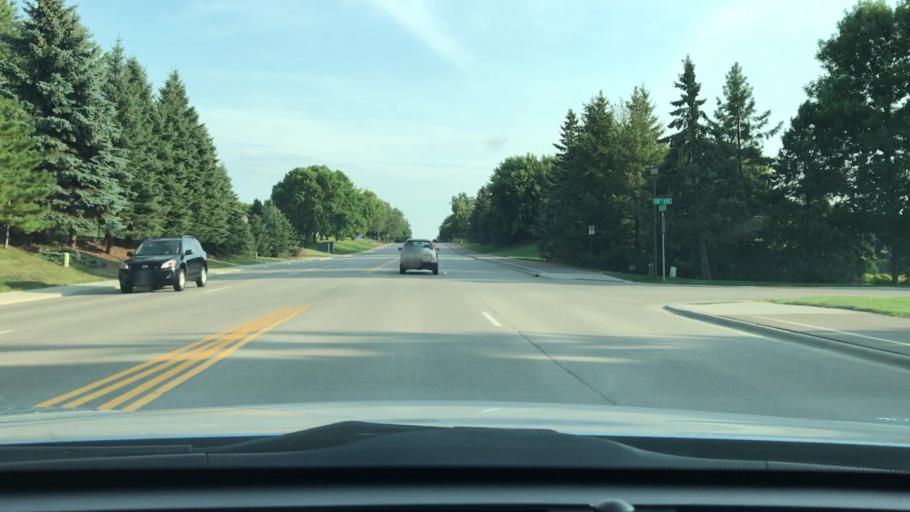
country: US
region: Minnesota
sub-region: Hennepin County
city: Plymouth
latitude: 45.0412
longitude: -93.4818
